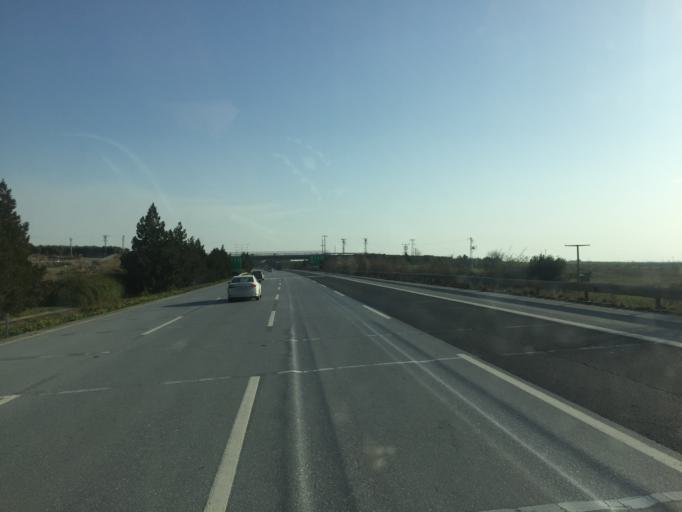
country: TR
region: Mersin
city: Yenice
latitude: 37.0245
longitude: 35.1022
